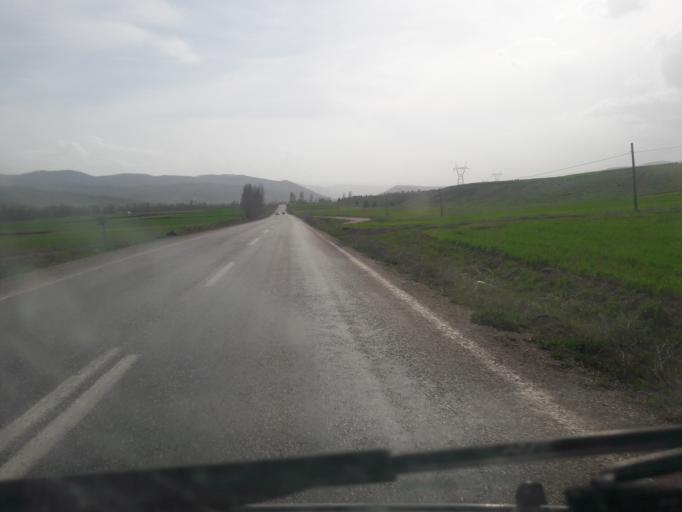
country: TR
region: Gumushane
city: Kelkit
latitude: 40.1372
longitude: 39.3834
